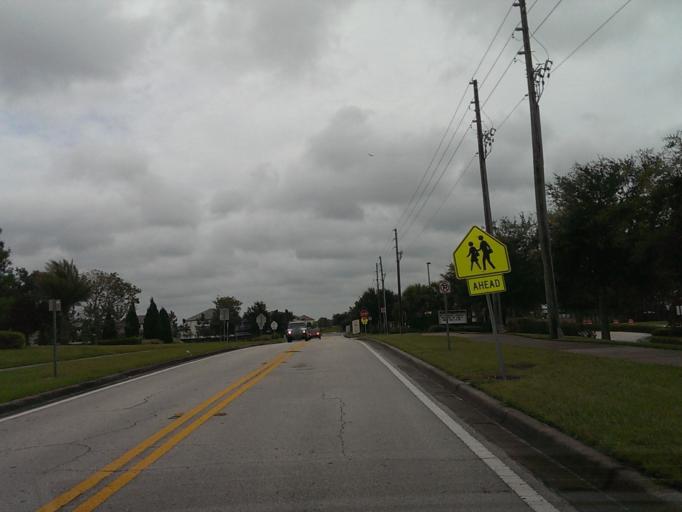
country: US
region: Florida
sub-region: Orange County
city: Windermere
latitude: 28.4606
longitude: -81.5599
